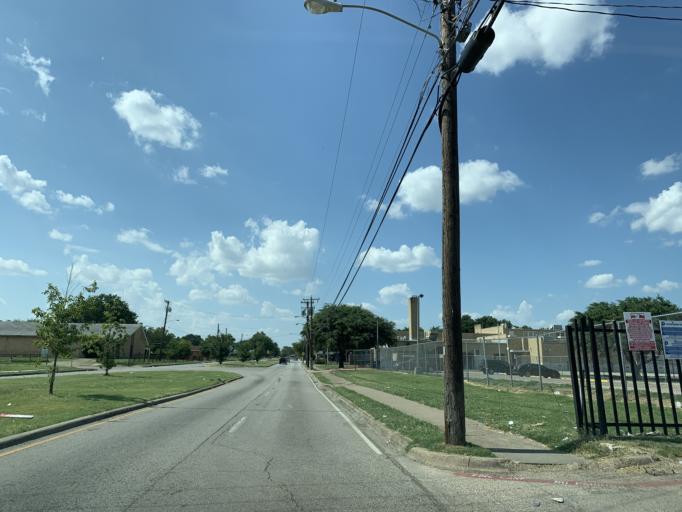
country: US
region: Texas
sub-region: Dallas County
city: Hutchins
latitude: 32.6967
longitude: -96.7734
